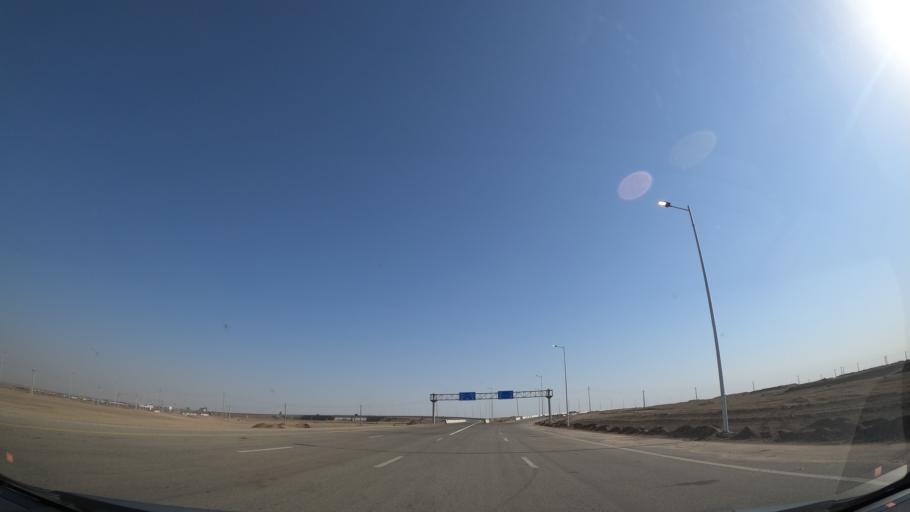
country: IR
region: Tehran
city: Eqbaliyeh
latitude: 35.1365
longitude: 51.5071
